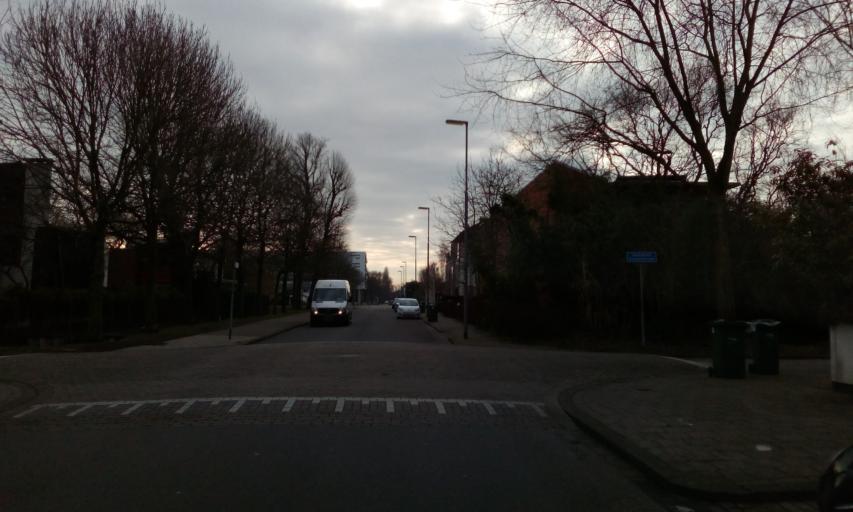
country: NL
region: South Holland
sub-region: Gemeente Rotterdam
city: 's-Gravenland
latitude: 51.9325
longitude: 4.5598
